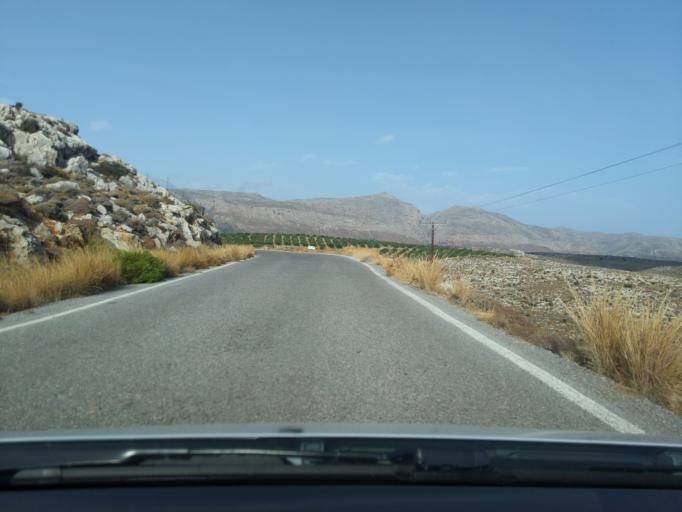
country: GR
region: Crete
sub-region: Nomos Lasithiou
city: Palekastro
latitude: 35.0862
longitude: 26.2491
